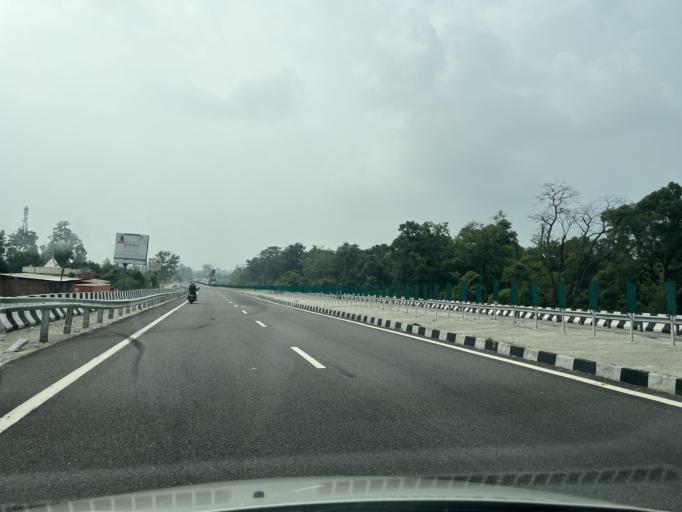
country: IN
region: Uttarakhand
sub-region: Dehradun
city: Raiwala
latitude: 30.0648
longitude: 78.2097
